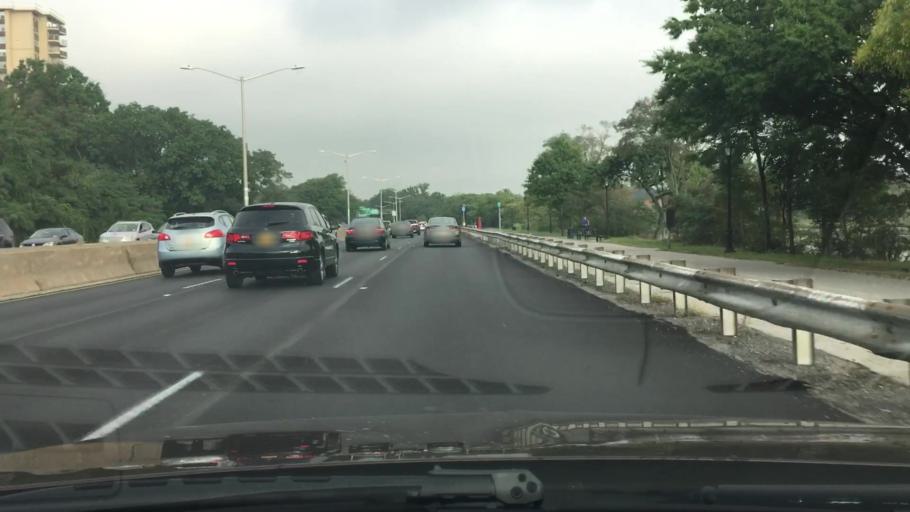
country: US
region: New York
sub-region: Nassau County
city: East Atlantic Beach
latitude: 40.7844
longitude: -73.7731
